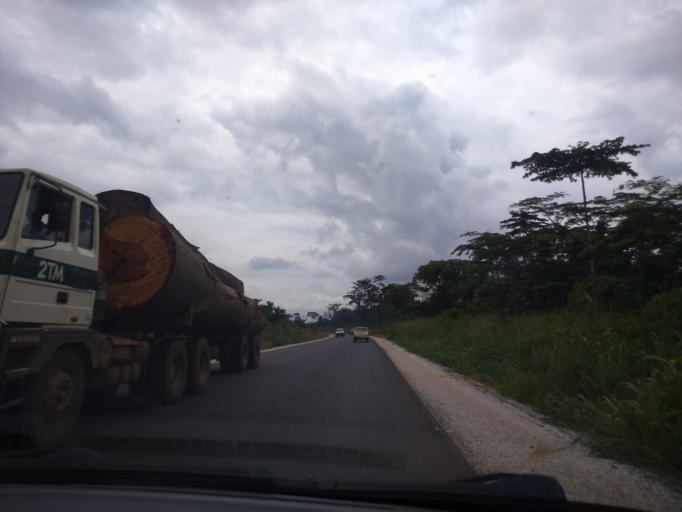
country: CI
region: Lagunes
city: Akoupe
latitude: 6.3160
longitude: -3.8314
